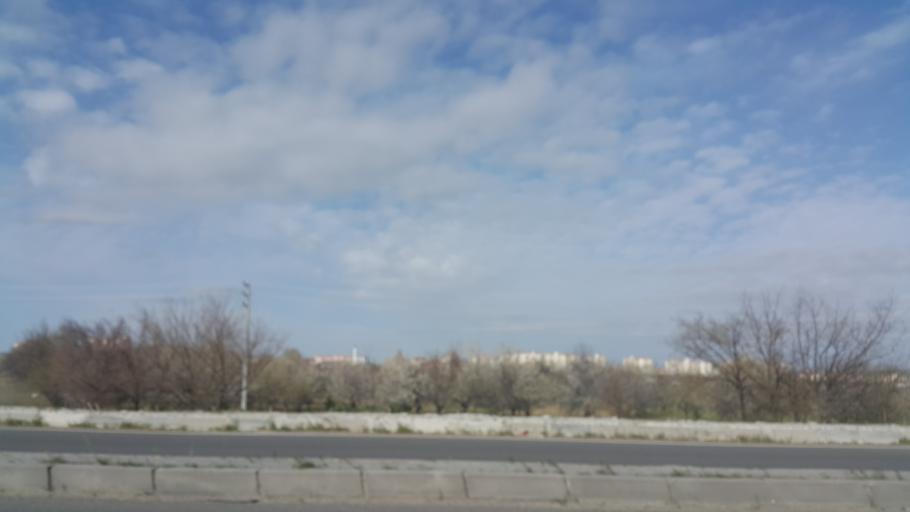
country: TR
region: Aksaray
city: Aksaray
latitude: 38.4102
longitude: 33.9759
